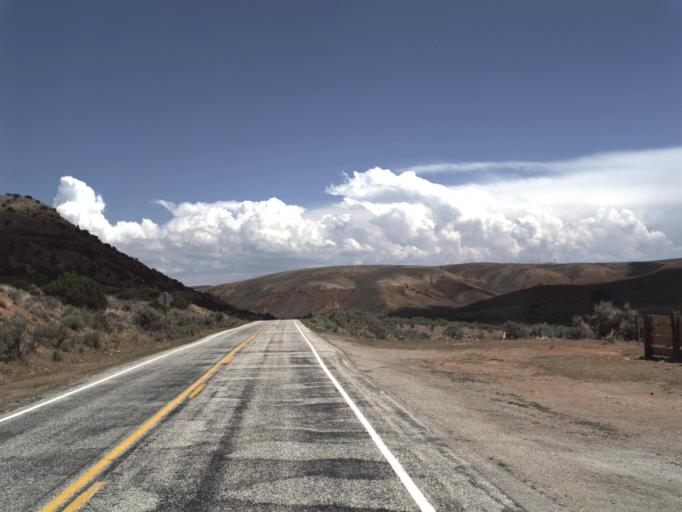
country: US
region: Utah
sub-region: Rich County
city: Randolph
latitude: 41.5005
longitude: -111.2782
